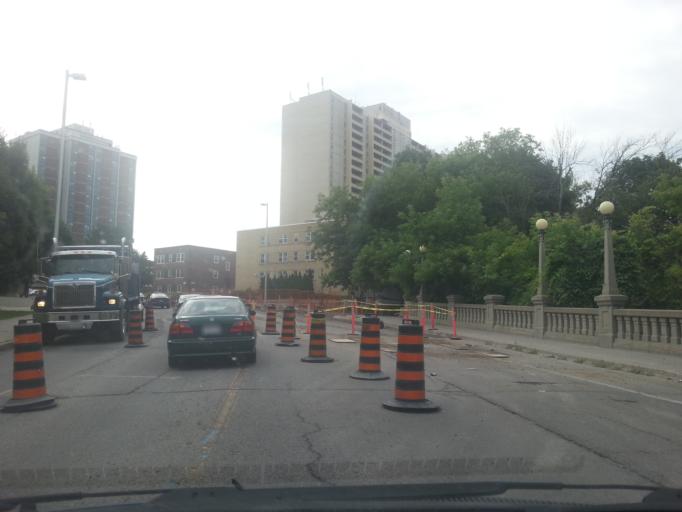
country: CA
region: Ontario
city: Ottawa
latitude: 45.4336
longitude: -75.6728
